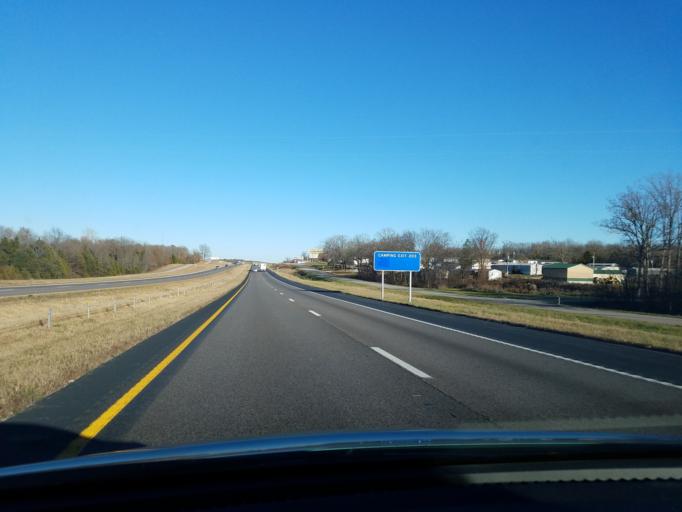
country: US
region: Missouri
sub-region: Crawford County
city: Cuba
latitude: 38.0403
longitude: -91.5073
